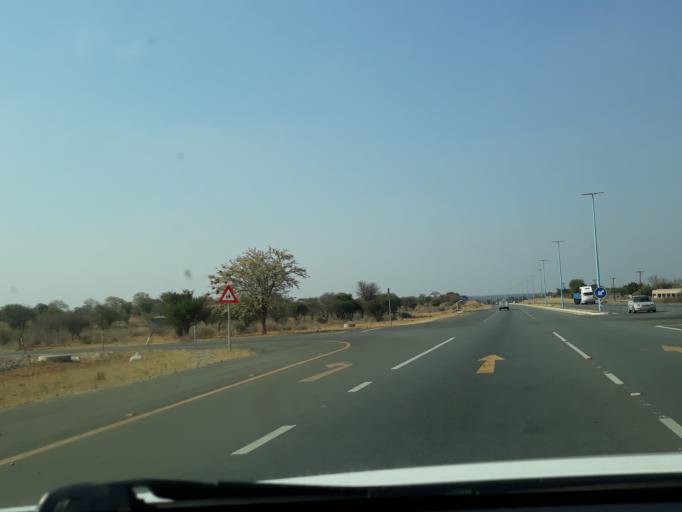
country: BW
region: Central
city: Tonota
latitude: -21.4181
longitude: 27.4456
